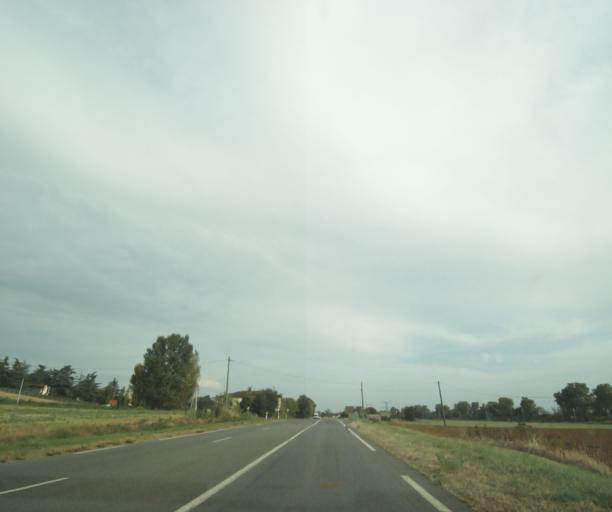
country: FR
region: Midi-Pyrenees
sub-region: Departement de la Haute-Garonne
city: Castelnau-d'Estretefonds
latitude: 43.7964
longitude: 1.3348
